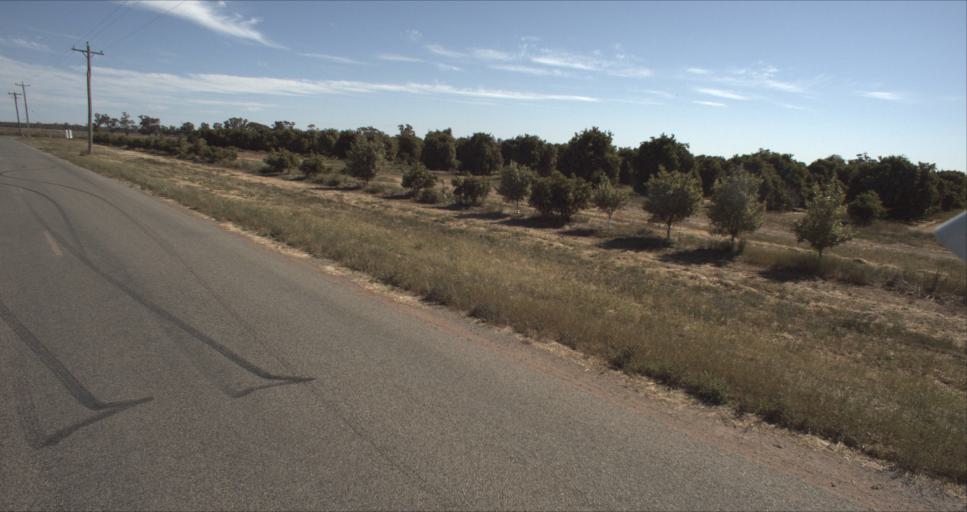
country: AU
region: New South Wales
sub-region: Leeton
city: Leeton
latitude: -34.5864
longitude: 146.3788
